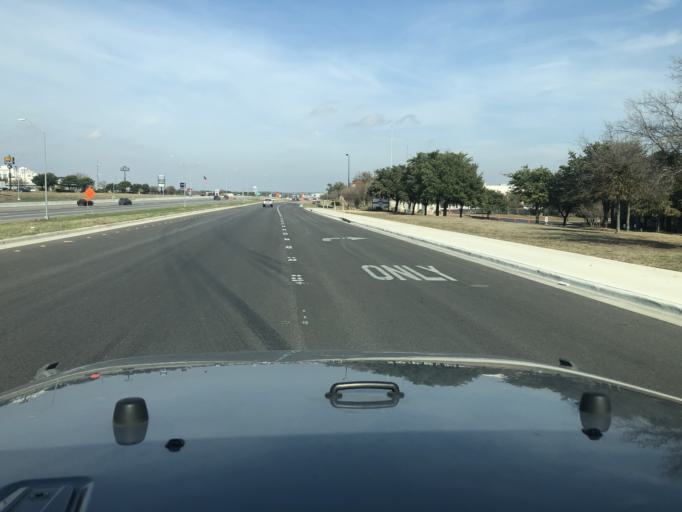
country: US
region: Texas
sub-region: Williamson County
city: Round Rock
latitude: 30.5371
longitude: -97.6916
